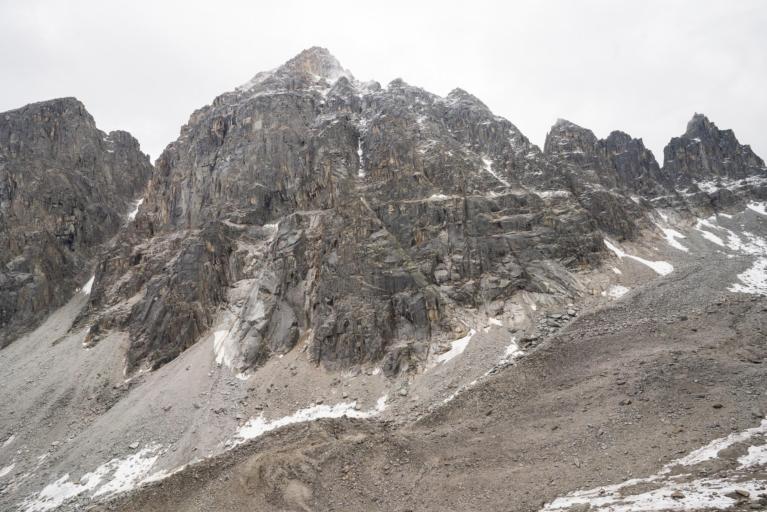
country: RU
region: Transbaikal Territory
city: Chara
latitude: 56.8706
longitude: 117.5675
